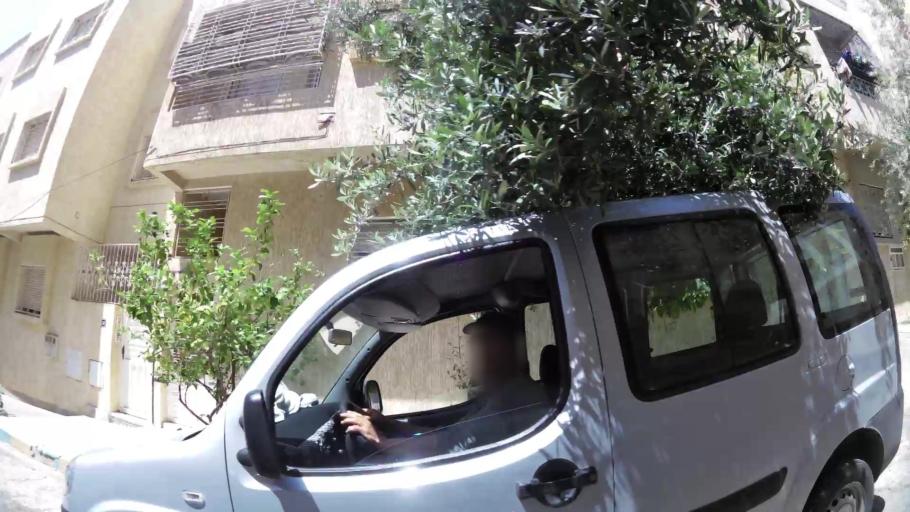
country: MA
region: Fes-Boulemane
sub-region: Fes
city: Fes
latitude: 34.0613
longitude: -5.0309
